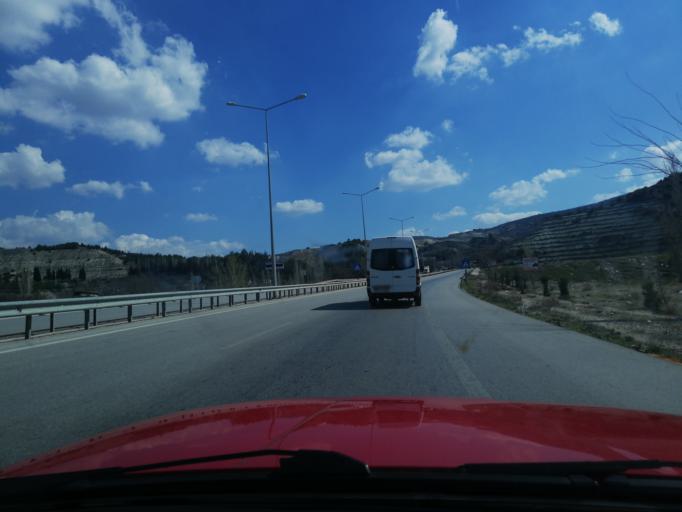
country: TR
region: Burdur
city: Burdur
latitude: 37.7068
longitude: 30.3056
